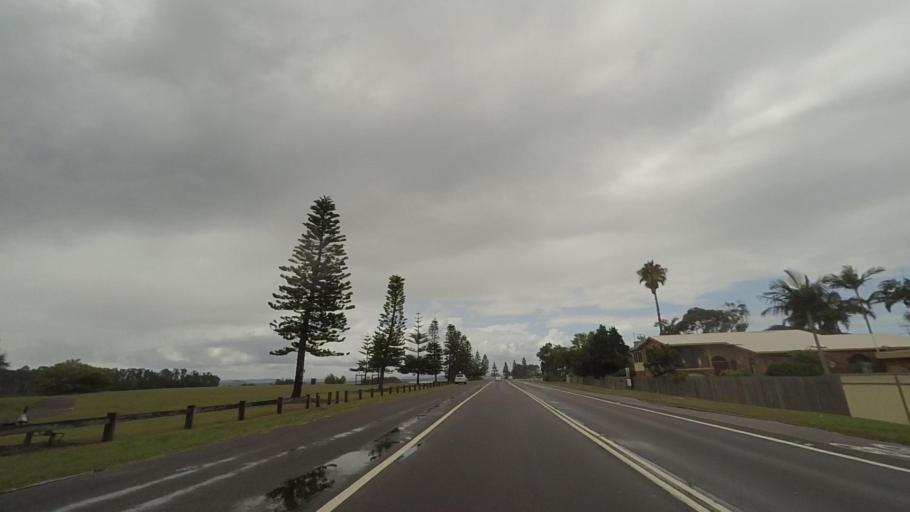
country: AU
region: New South Wales
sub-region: Wyong Shire
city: The Entrance
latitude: -33.3314
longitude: 151.5030
